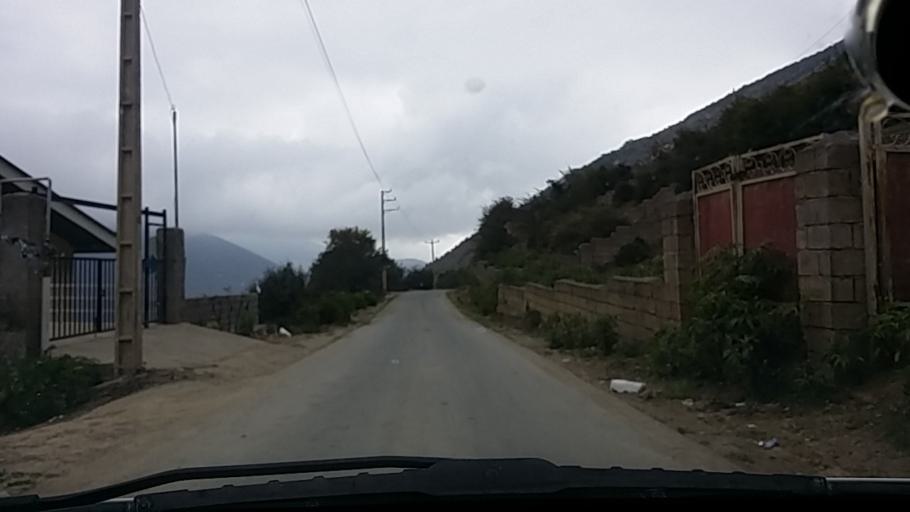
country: IR
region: Mazandaran
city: `Abbasabad
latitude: 36.4704
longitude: 51.1398
